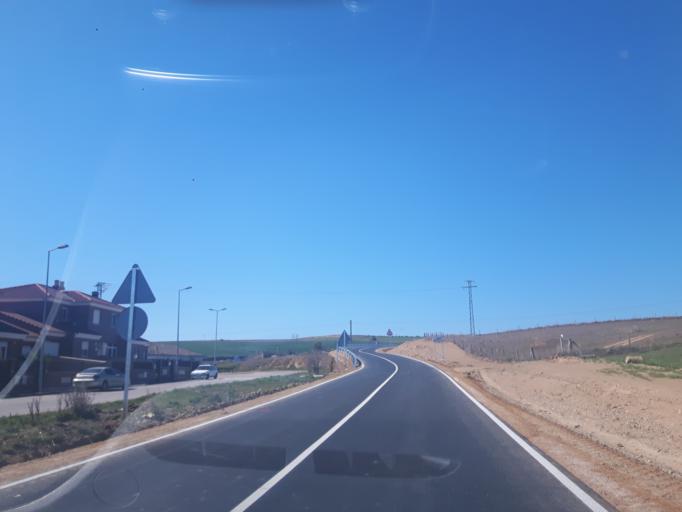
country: ES
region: Castille and Leon
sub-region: Provincia de Salamanca
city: Alba de Tormes
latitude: 40.8247
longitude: -5.5234
